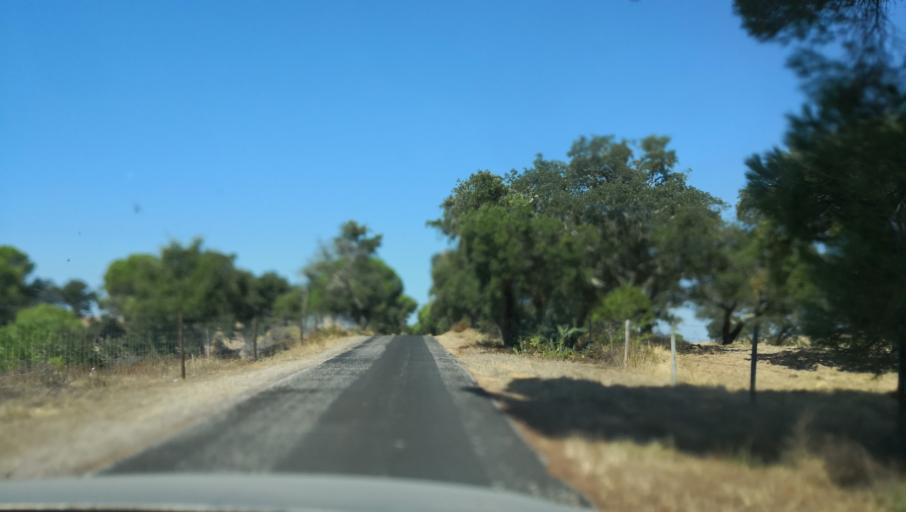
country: PT
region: Setubal
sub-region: Alcacer do Sal
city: Alcacer do Sal
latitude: 38.2537
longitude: -8.2994
